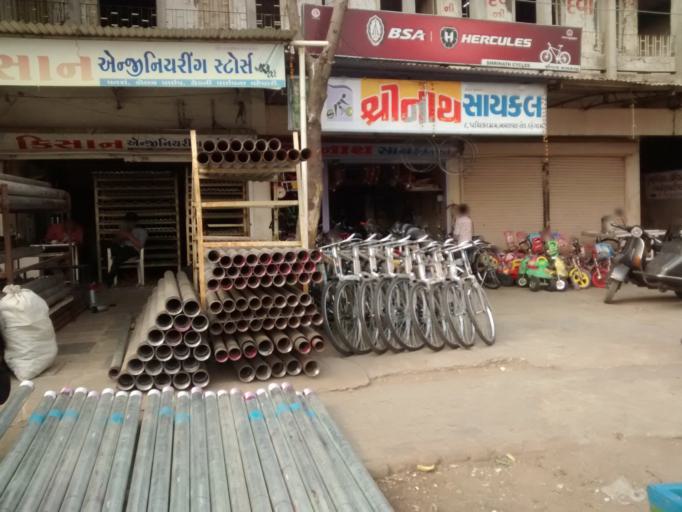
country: IN
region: Gujarat
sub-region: Gandhinagar
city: Dahegam
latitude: 23.1700
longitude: 72.8197
